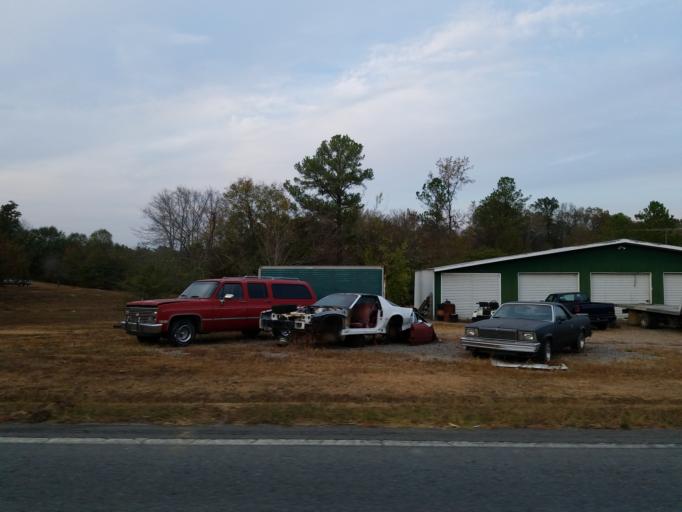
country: US
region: Georgia
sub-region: Gordon County
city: Calhoun
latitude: 34.5943
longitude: -84.9064
